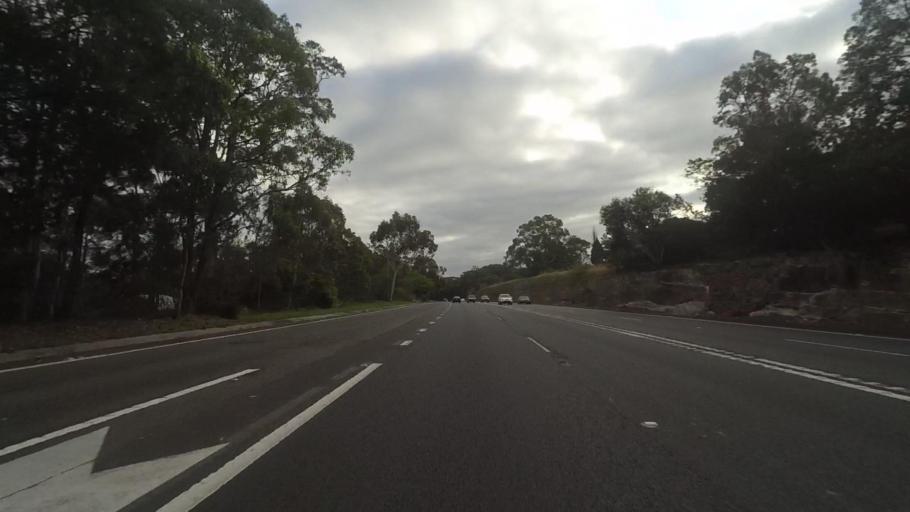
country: AU
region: New South Wales
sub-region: Sutherland Shire
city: Menai
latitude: -34.0047
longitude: 151.0156
